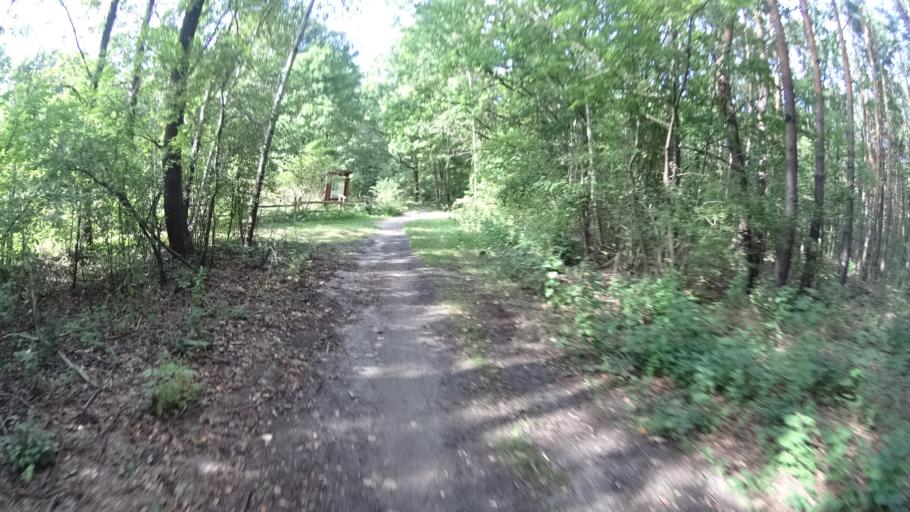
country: PL
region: Masovian Voivodeship
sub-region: Powiat warszawski zachodni
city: Babice
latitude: 52.2726
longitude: 20.8716
